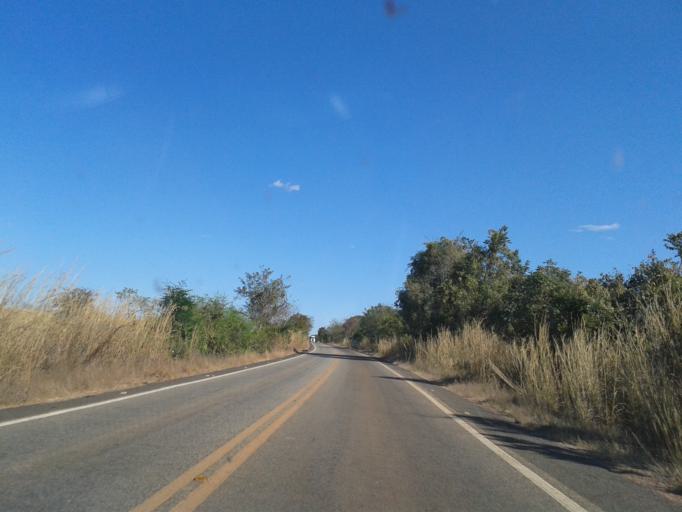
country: BR
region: Goias
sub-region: Mozarlandia
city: Mozarlandia
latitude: -14.6205
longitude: -50.5183
